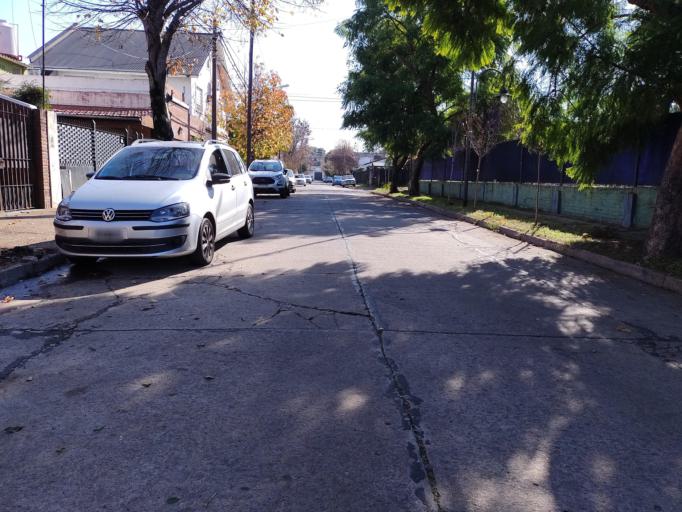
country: AR
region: Buenos Aires
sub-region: Partido de San Isidro
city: San Isidro
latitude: -34.4498
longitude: -58.5391
